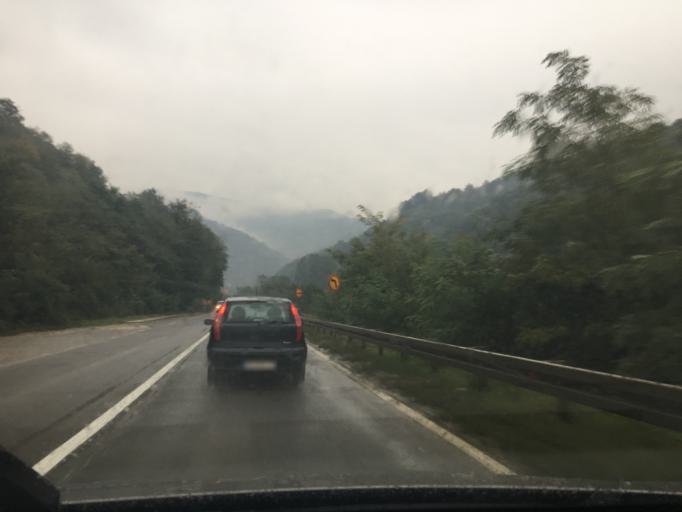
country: RS
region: Central Serbia
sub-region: Pcinjski Okrug
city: Vladicin Han
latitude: 42.7502
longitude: 22.0692
